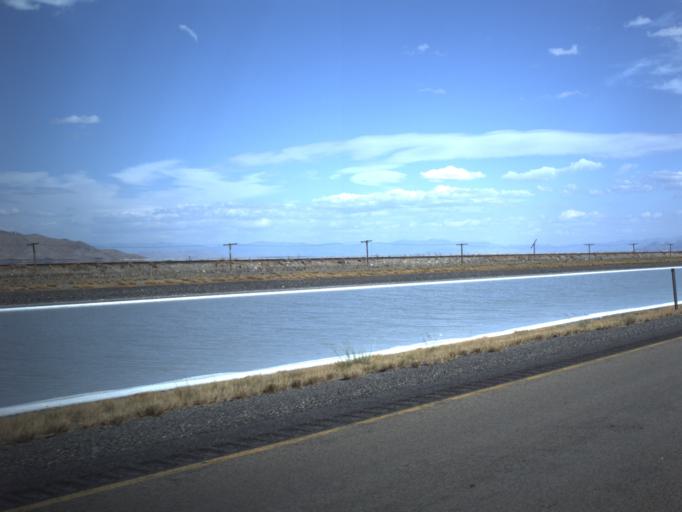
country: US
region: Utah
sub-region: Tooele County
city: Grantsville
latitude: 40.7339
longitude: -112.6028
